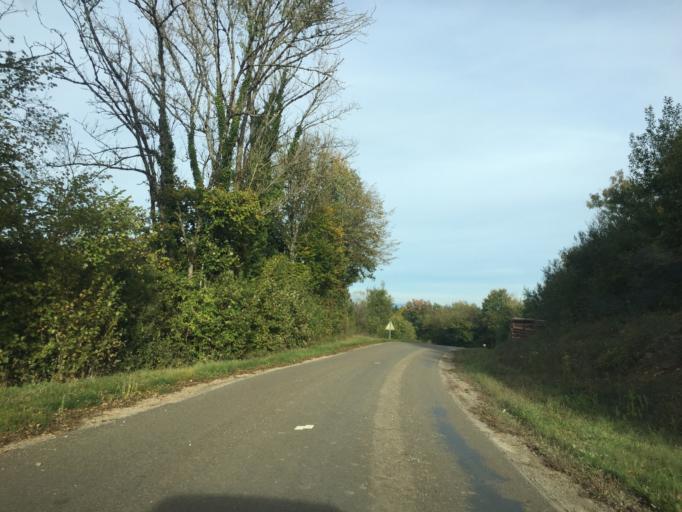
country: FR
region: Franche-Comte
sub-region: Departement du Jura
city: Orgelet
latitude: 46.4987
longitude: 5.5107
